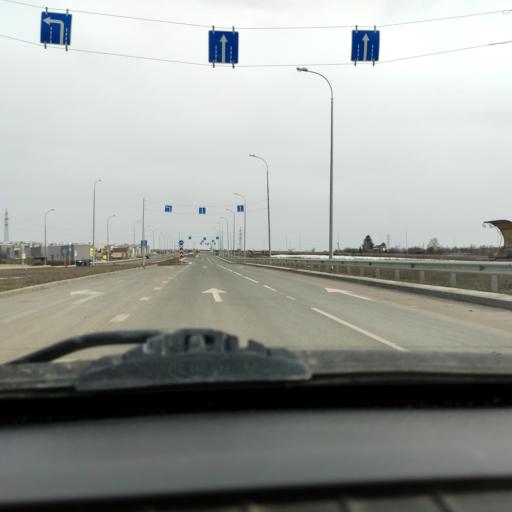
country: RU
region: Samara
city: Petra-Dubrava
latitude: 53.2936
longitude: 50.3296
